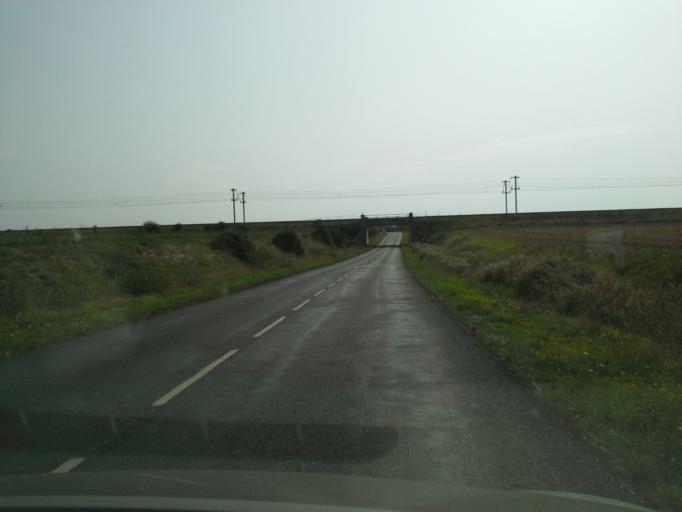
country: FR
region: Centre
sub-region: Departement du Loir-et-Cher
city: La Ville-aux-Clercs
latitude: 47.9090
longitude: 1.0542
